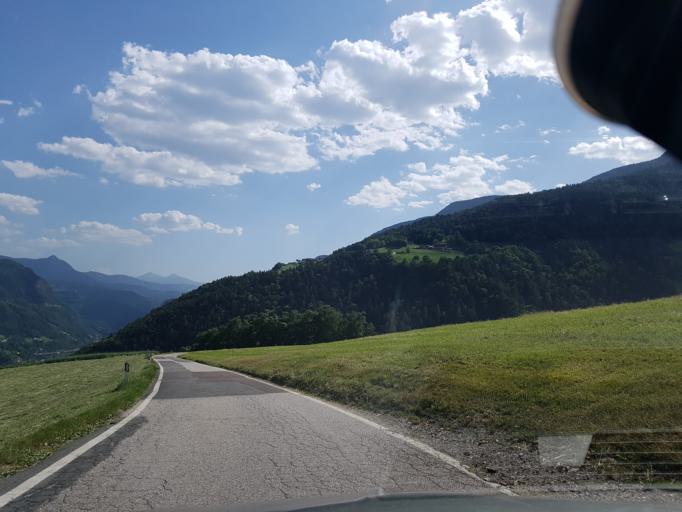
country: IT
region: Trentino-Alto Adige
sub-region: Bolzano
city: Villandro - Villanders
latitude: 46.6227
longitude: 11.5320
